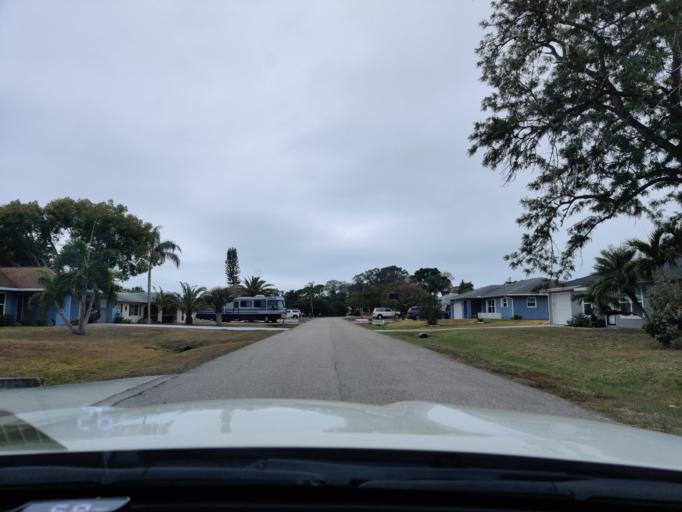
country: US
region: Florida
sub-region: Sarasota County
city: South Venice
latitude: 27.0423
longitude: -82.4084
